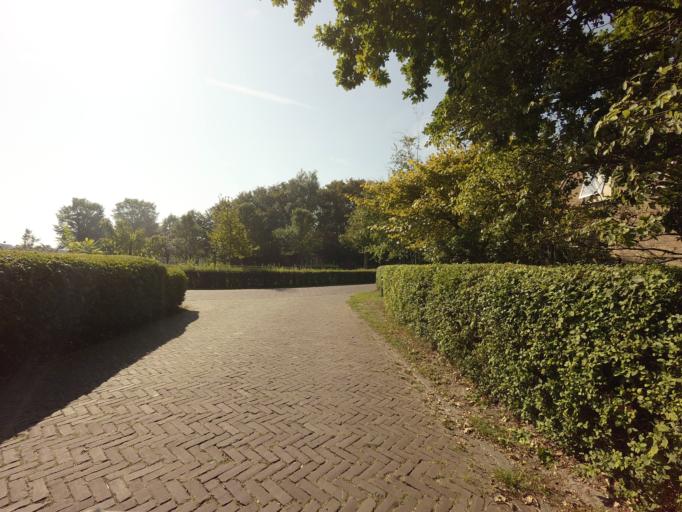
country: NL
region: Friesland
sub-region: Gemeente Schiermonnikoog
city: Schiermonnikoog
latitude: 53.4808
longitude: 6.1669
